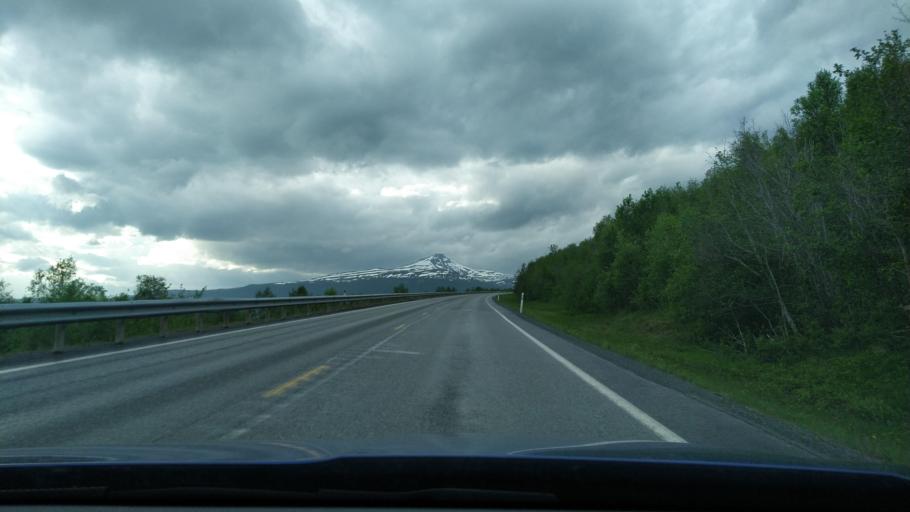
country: NO
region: Troms
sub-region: Balsfjord
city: Storsteinnes
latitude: 69.2418
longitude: 19.4567
